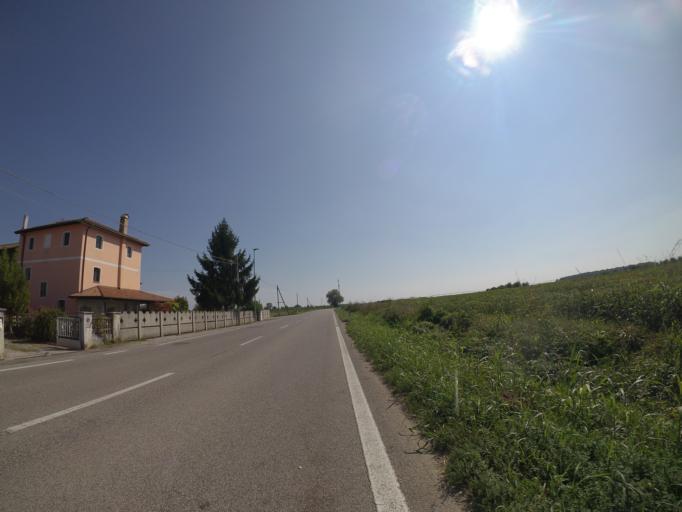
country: IT
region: Friuli Venezia Giulia
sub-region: Provincia di Udine
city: Carlino
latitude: 45.8034
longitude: 13.1657
